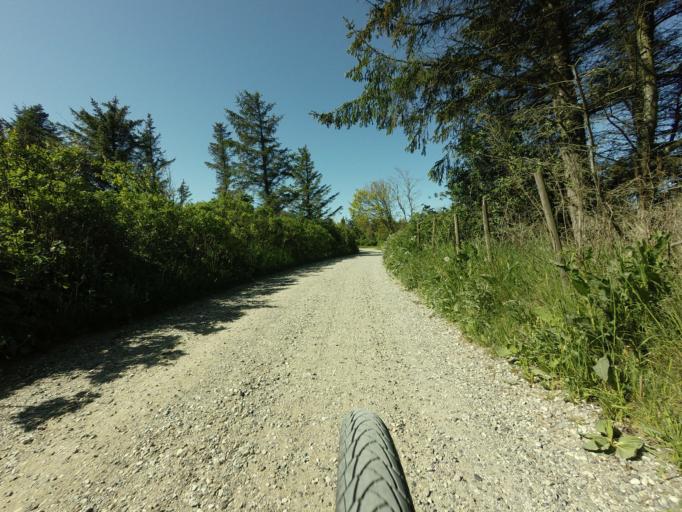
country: DK
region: North Denmark
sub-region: Jammerbugt Kommune
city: Pandrup
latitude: 57.3242
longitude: 9.6707
